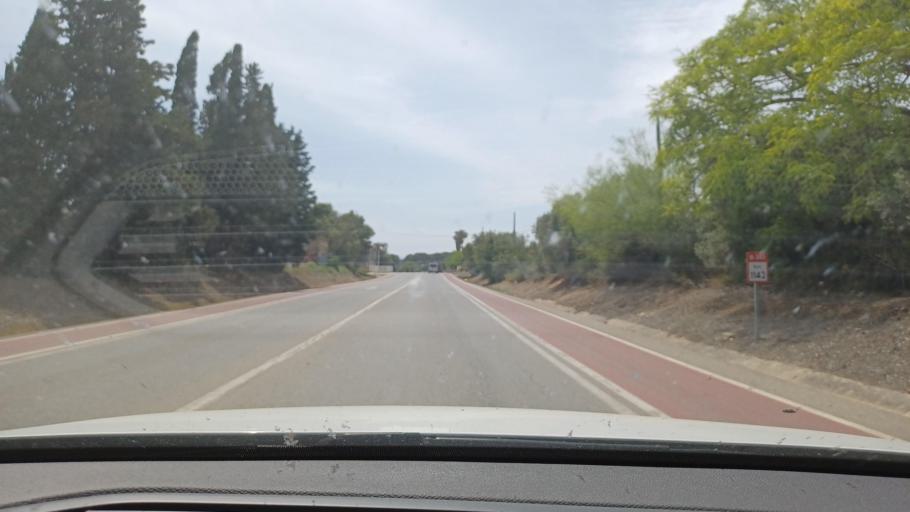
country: ES
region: Catalonia
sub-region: Provincia de Tarragona
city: Cambrils
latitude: 41.0685
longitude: 1.0417
